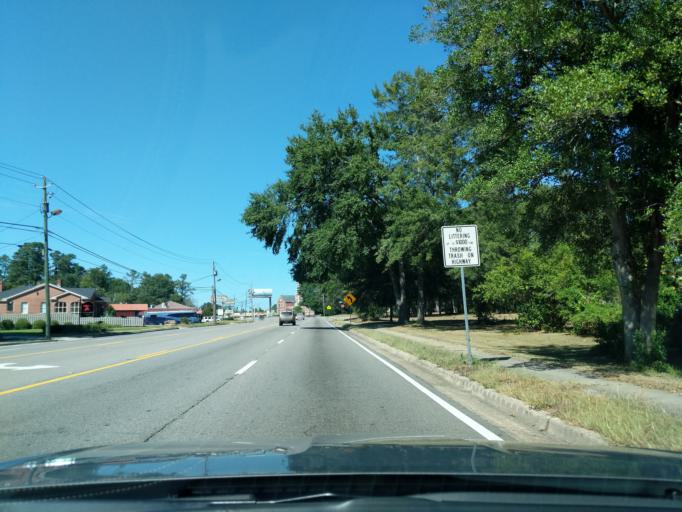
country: US
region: Georgia
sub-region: Richmond County
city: Augusta
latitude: 33.4971
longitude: -82.0110
